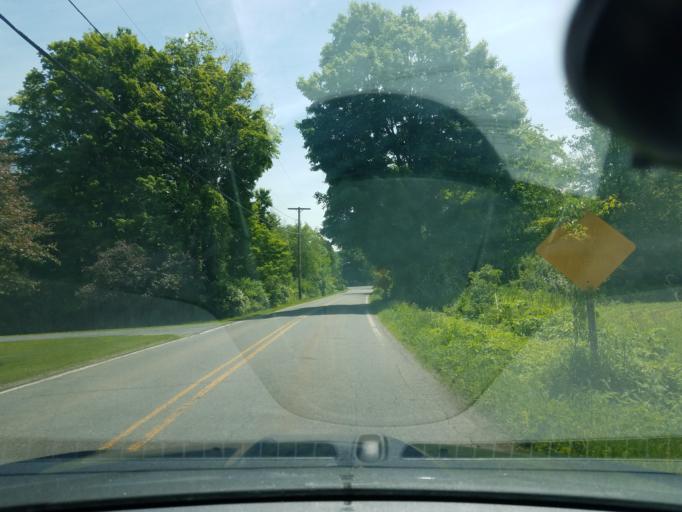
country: US
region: Connecticut
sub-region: Litchfield County
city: Canaan
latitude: 42.0473
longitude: -73.2906
